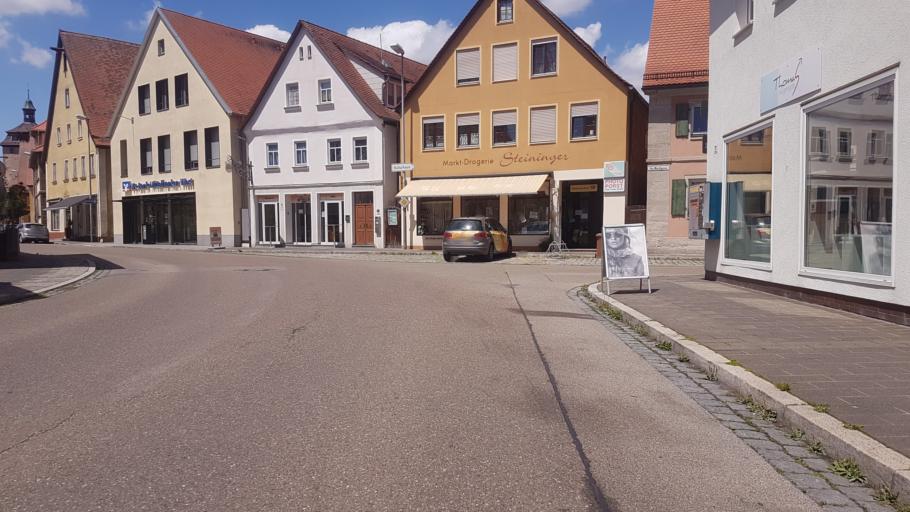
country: DE
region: Bavaria
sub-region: Regierungsbezirk Mittelfranken
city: Leutershausen
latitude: 49.2996
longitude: 10.4090
